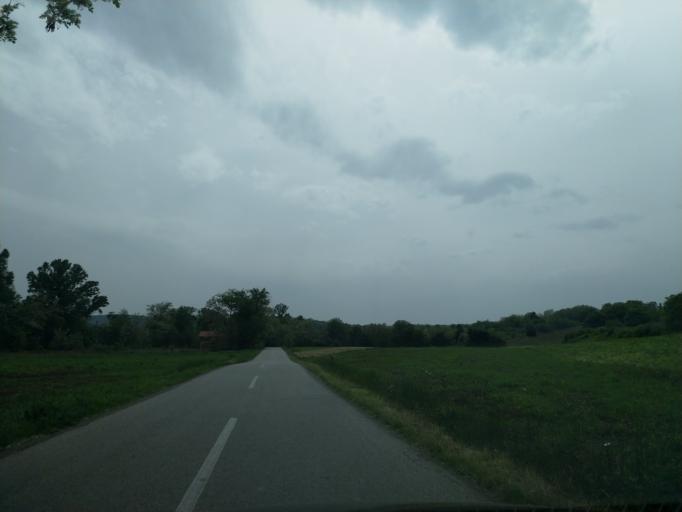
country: RS
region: Central Serbia
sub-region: Pomoravski Okrug
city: Paracin
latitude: 43.8684
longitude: 21.5404
